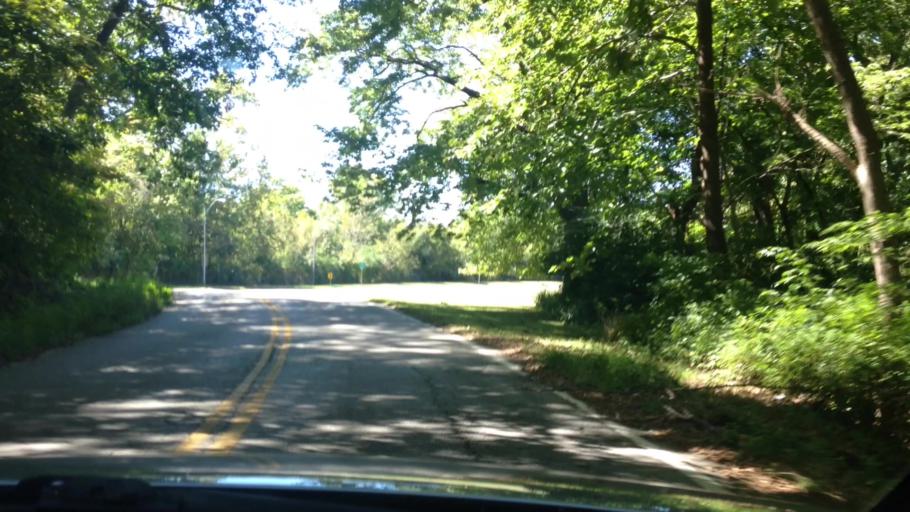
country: US
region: Missouri
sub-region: Jackson County
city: Raytown
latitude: 39.0051
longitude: -94.5171
